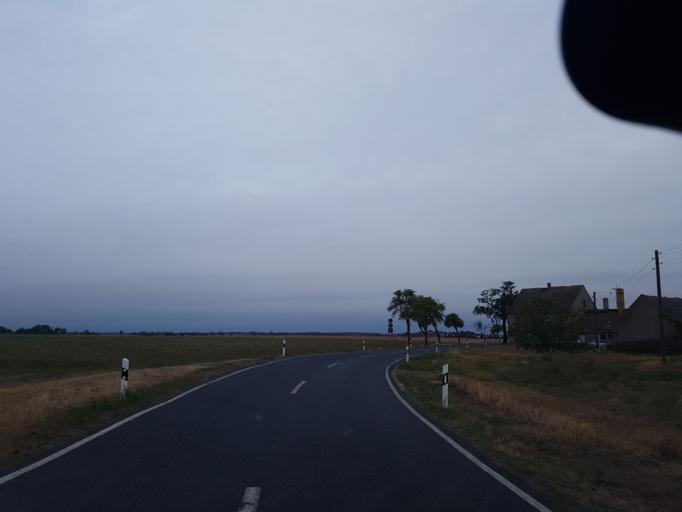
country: DE
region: Saxony
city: Arzberg
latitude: 51.5134
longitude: 13.1527
